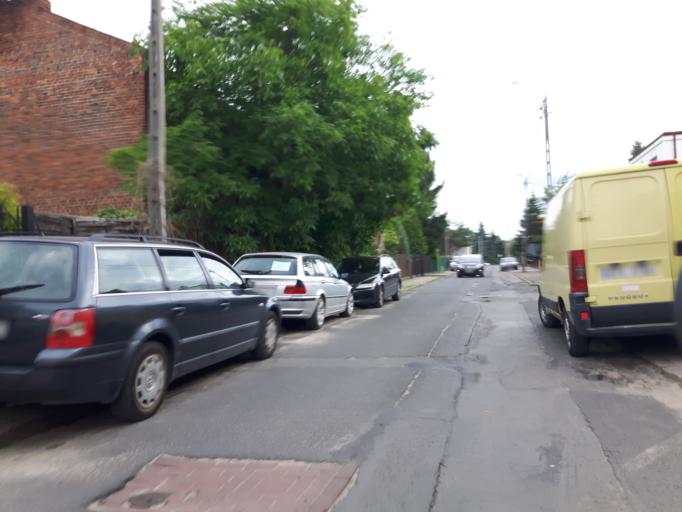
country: PL
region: Masovian Voivodeship
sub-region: Powiat wolominski
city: Zabki
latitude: 52.2854
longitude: 21.1158
